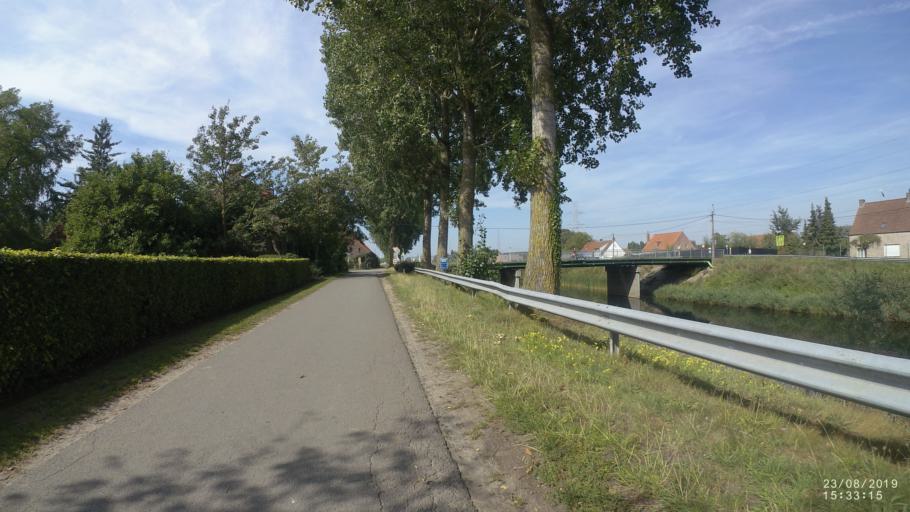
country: BE
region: Flanders
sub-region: Provincie Oost-Vlaanderen
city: Eeklo
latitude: 51.1585
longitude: 3.5470
